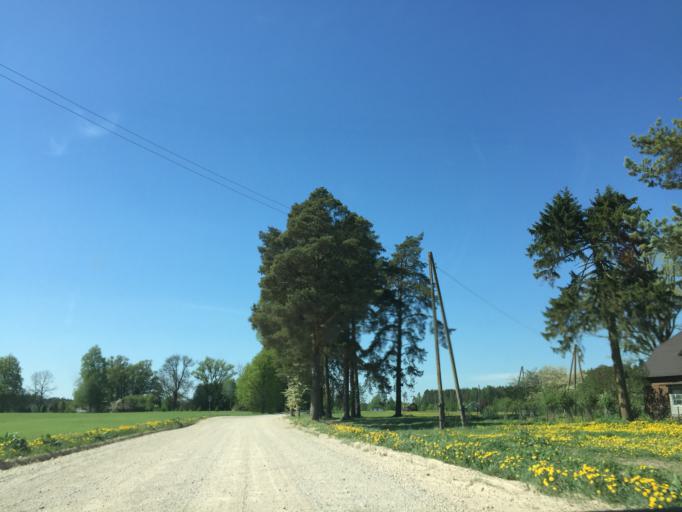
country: LV
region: Kegums
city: Kegums
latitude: 56.8537
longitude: 24.7291
